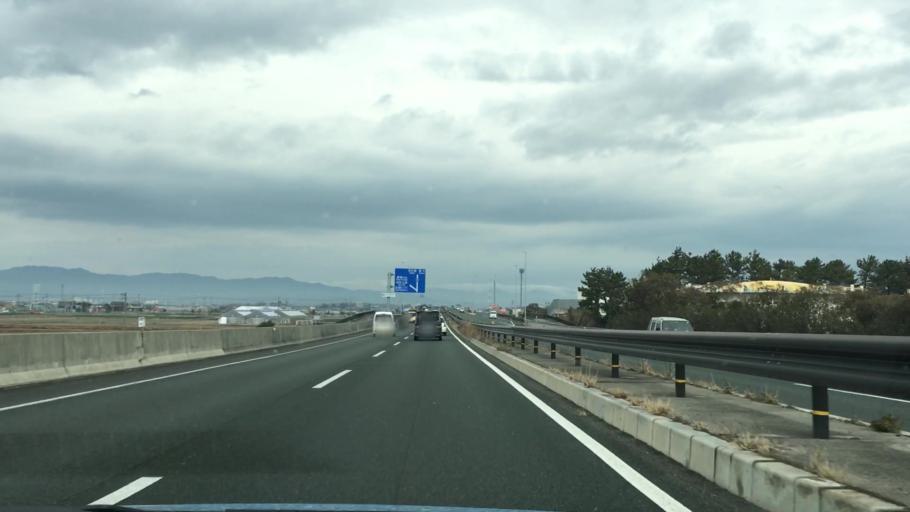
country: JP
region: Aichi
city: Toyohashi
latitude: 34.7561
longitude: 137.3340
